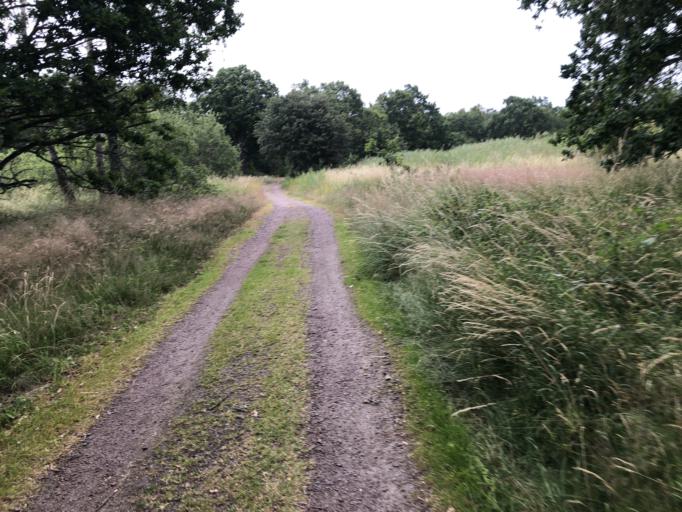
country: SE
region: Kalmar
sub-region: Kalmar Kommun
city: Kalmar
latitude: 56.6389
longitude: 16.3217
